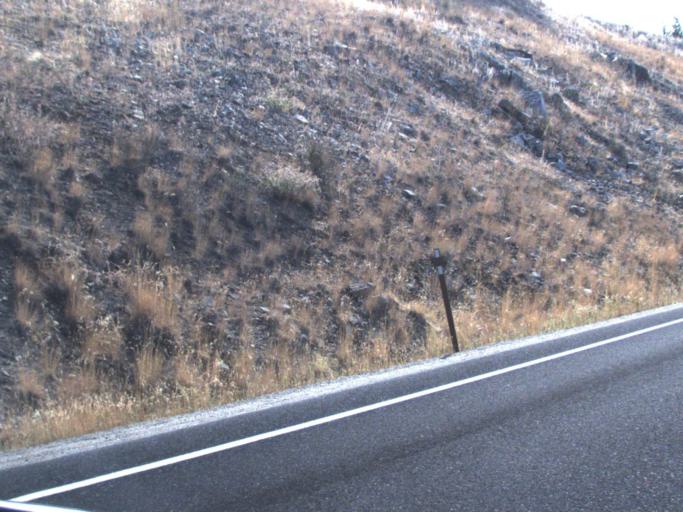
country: US
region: Washington
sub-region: Spokane County
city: Fairwood
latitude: 47.7746
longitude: -117.5428
